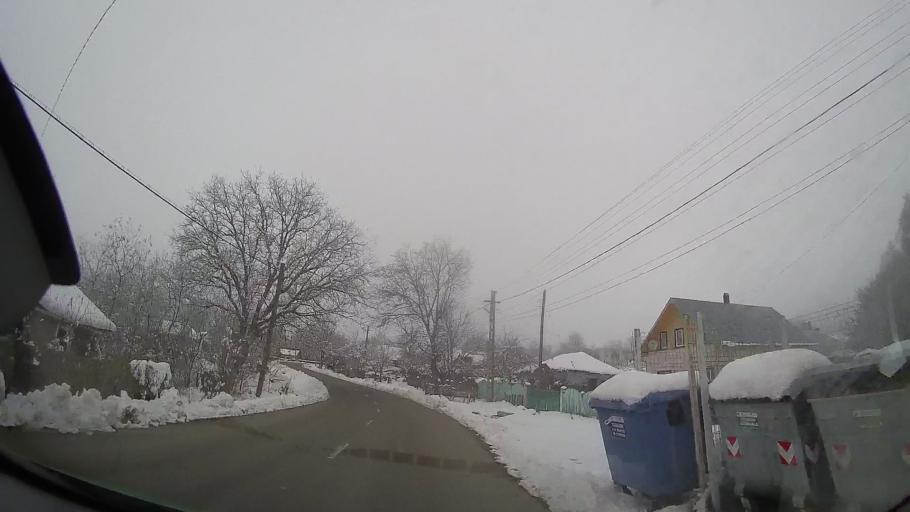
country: RO
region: Neamt
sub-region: Comuna Bozieni
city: Bozieni
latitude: 46.8377
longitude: 27.1530
